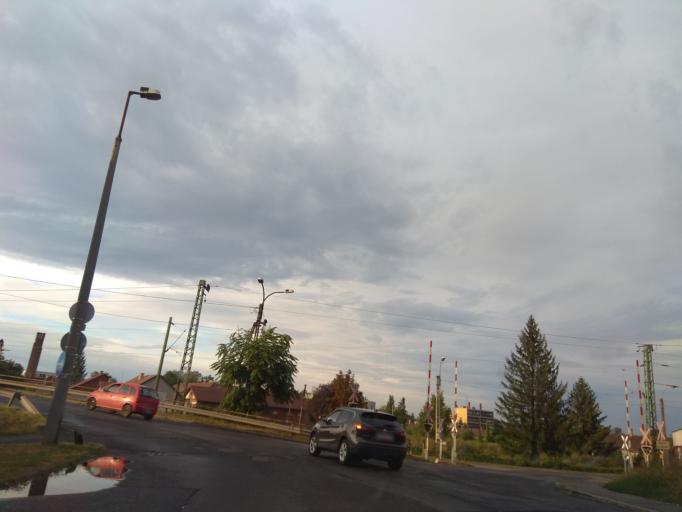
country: HU
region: Borsod-Abauj-Zemplen
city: Miskolc
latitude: 48.0980
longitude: 20.8029
